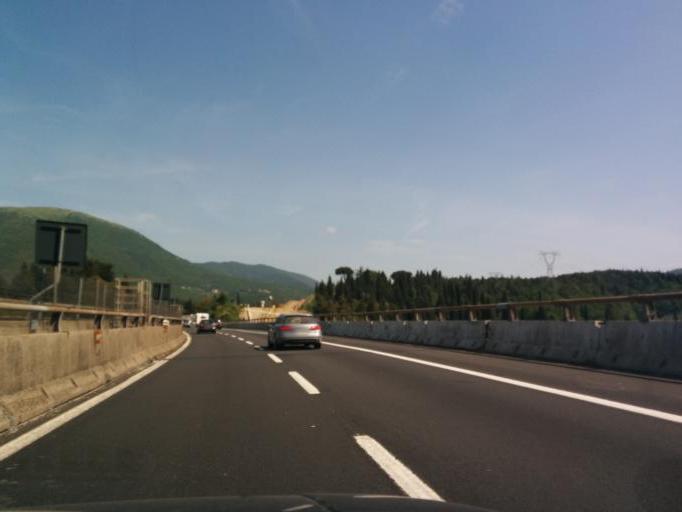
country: IT
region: Tuscany
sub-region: Province of Florence
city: Carraia
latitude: 43.8854
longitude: 11.1850
